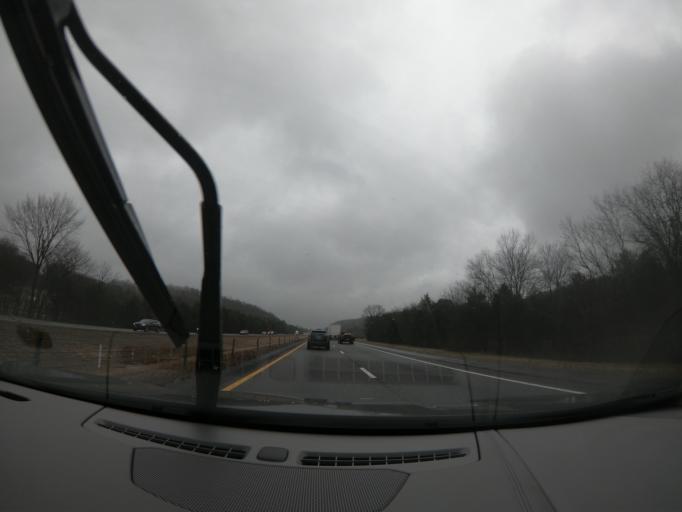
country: US
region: Tennessee
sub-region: Rutherford County
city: Plainview
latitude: 35.6447
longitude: -86.2529
